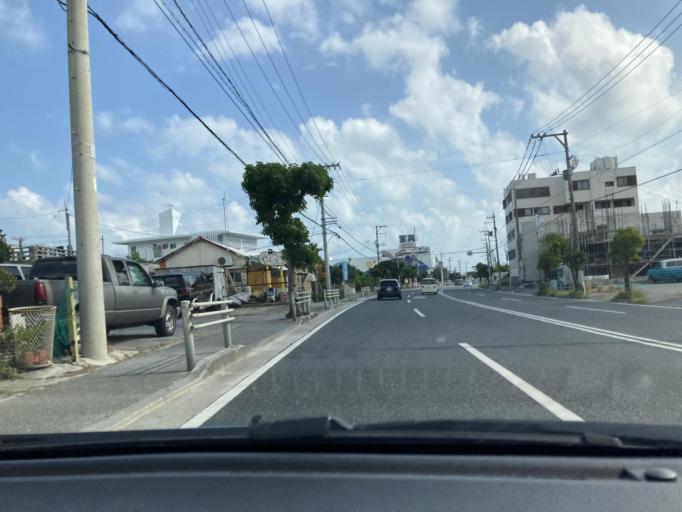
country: JP
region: Okinawa
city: Chatan
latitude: 26.2873
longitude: 127.8146
